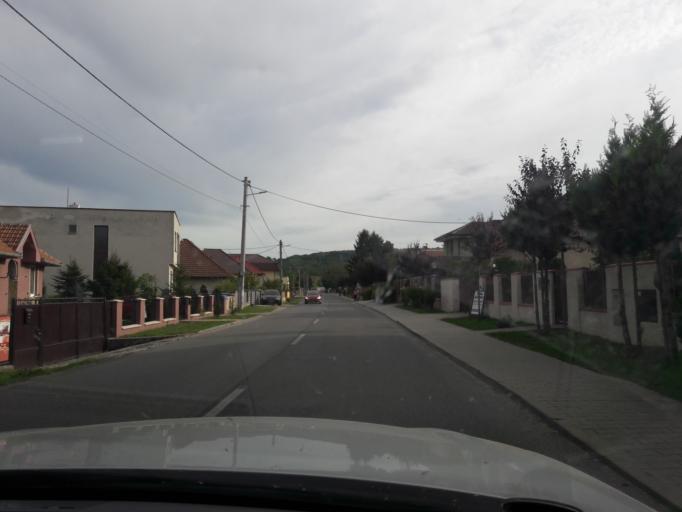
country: SK
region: Nitriansky
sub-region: Okres Nitra
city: Vrable
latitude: 48.1039
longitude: 18.3370
